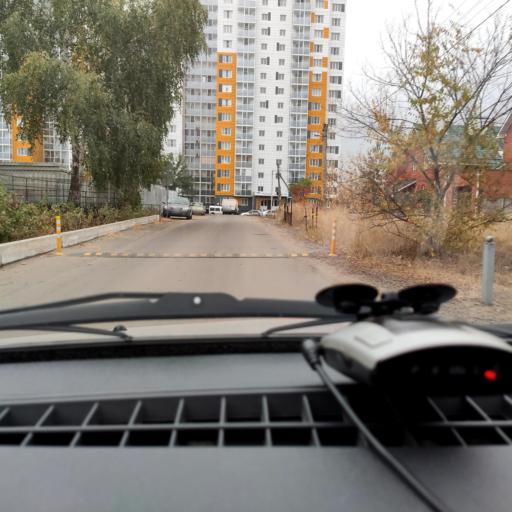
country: RU
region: Voronezj
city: Podgornoye
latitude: 51.7618
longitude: 39.1810
